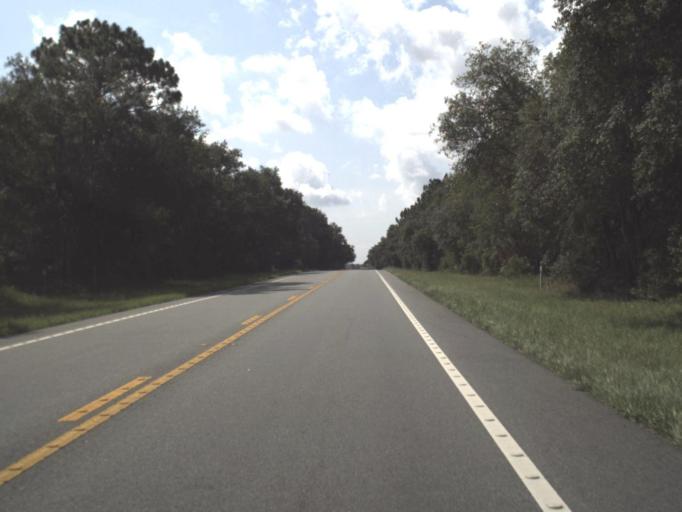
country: US
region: Florida
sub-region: Citrus County
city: Citrus Springs
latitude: 28.9851
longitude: -82.4340
